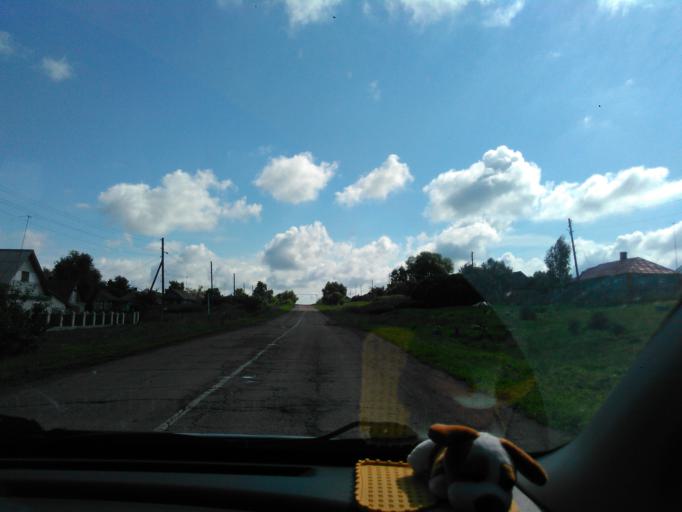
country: RU
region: Penza
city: Mokshan
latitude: 53.2542
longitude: 44.1489
